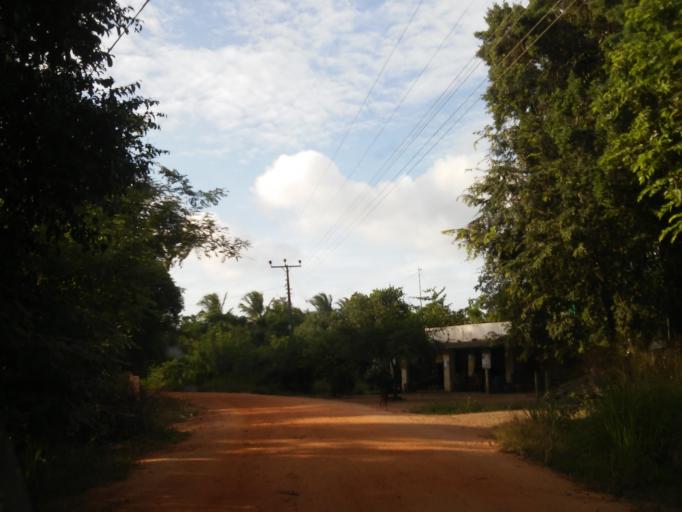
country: LK
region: Central
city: Sigiriya
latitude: 8.1753
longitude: 80.6685
